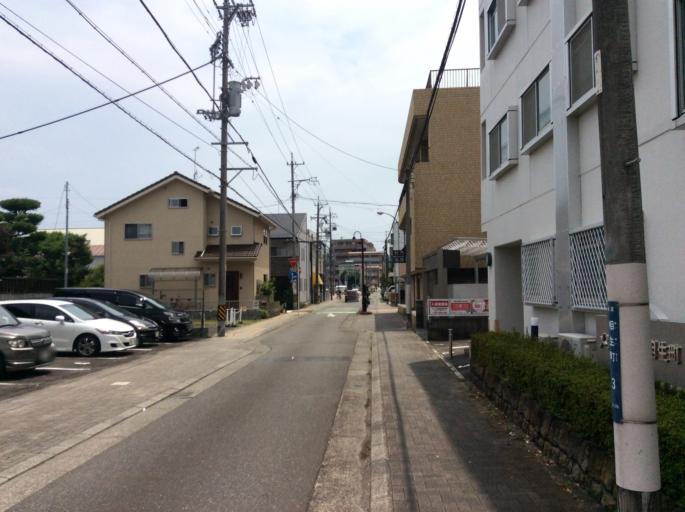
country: JP
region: Shizuoka
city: Shizuoka-shi
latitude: 34.9796
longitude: 138.3920
